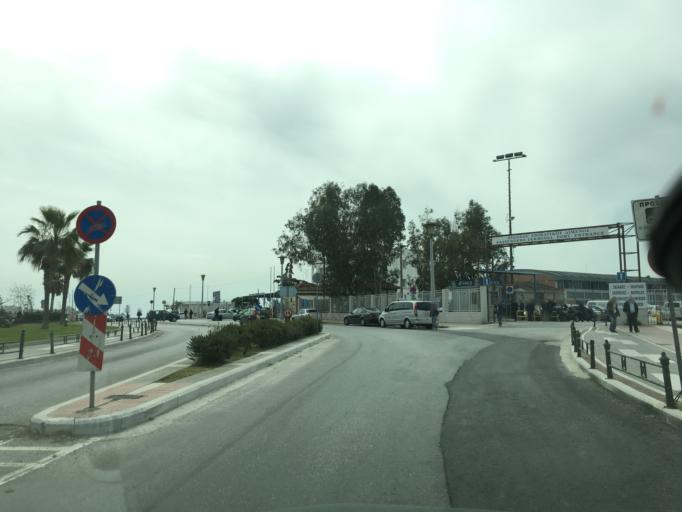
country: GR
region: Thessaly
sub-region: Nomos Magnisias
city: Volos
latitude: 39.3604
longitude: 22.9438
